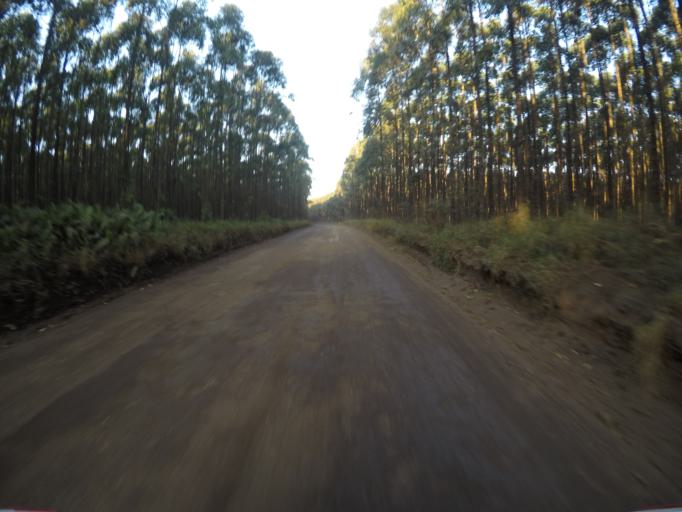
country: ZA
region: KwaZulu-Natal
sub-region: uThungulu District Municipality
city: KwaMbonambi
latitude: -28.6737
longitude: 32.0932
